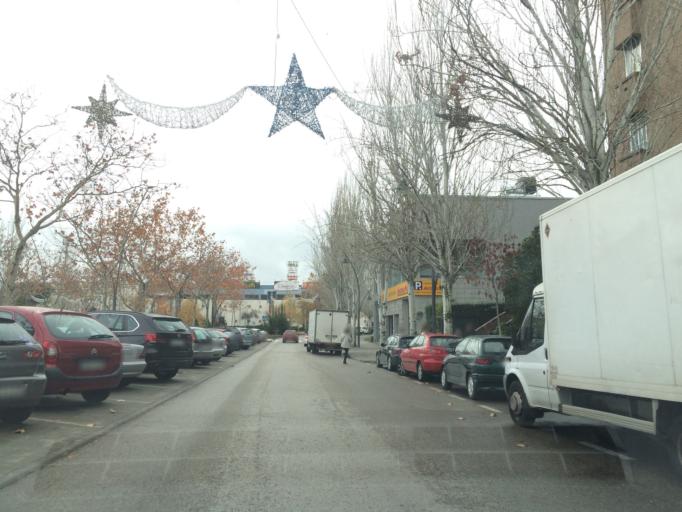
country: ES
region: Madrid
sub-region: Provincia de Madrid
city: Tres Cantos
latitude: 40.6070
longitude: -3.7160
